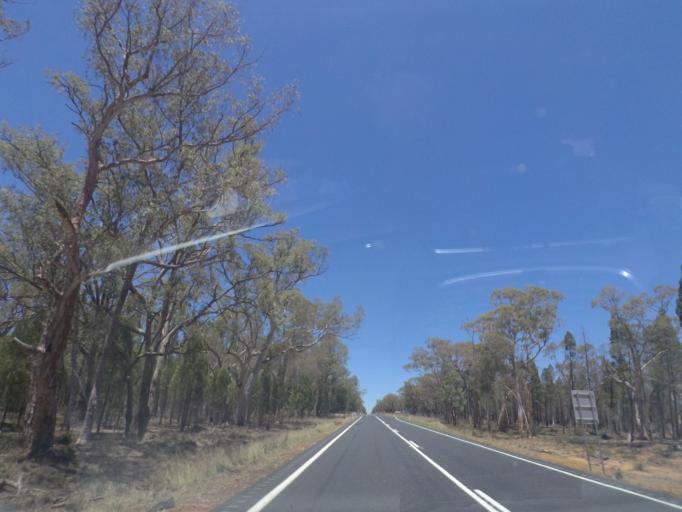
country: AU
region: New South Wales
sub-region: Warrumbungle Shire
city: Coonabarabran
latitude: -30.8529
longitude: 149.4574
